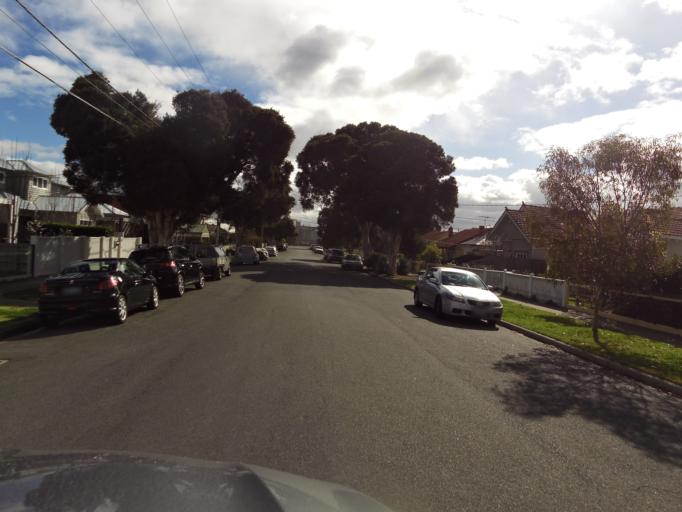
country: AU
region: Victoria
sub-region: Hobsons Bay
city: Newport
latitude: -37.8408
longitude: 144.8876
